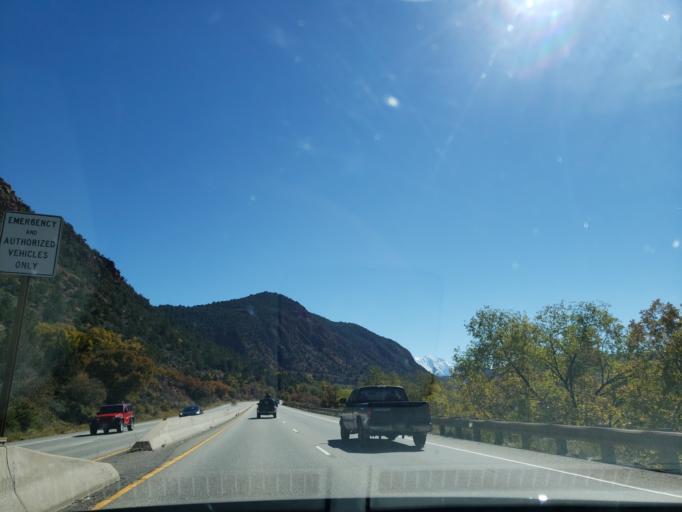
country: US
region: Colorado
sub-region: Garfield County
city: Glenwood Springs
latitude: 39.5116
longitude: -107.3075
